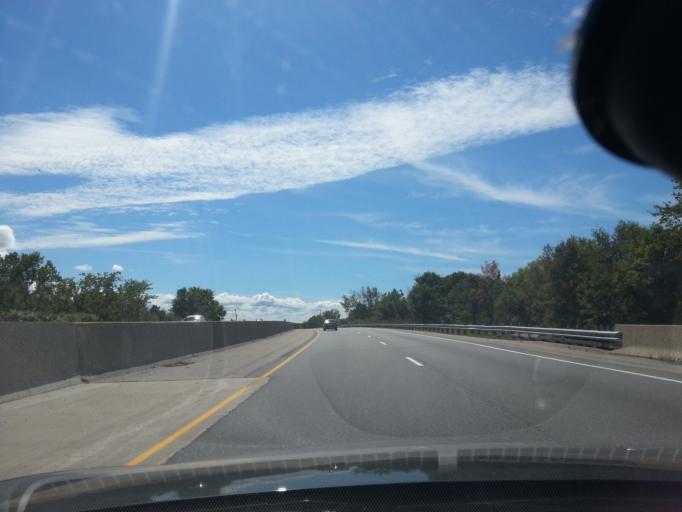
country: CA
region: Ontario
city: Brockville
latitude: 44.5801
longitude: -75.7336
